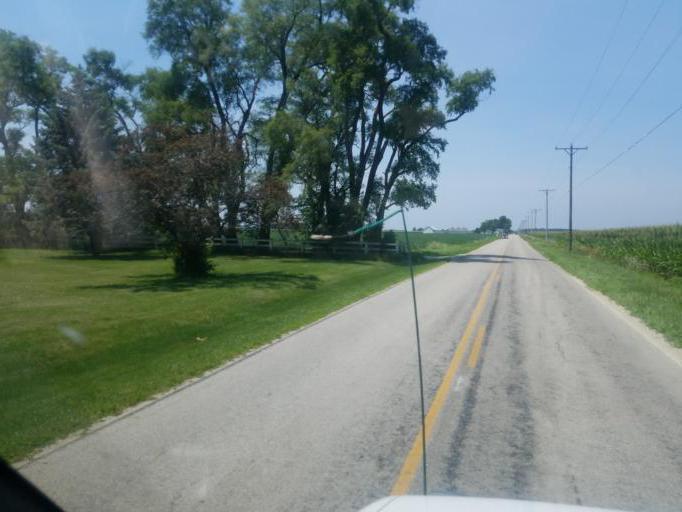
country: US
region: Ohio
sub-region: Shelby County
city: Sidney
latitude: 40.3032
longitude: -84.0608
